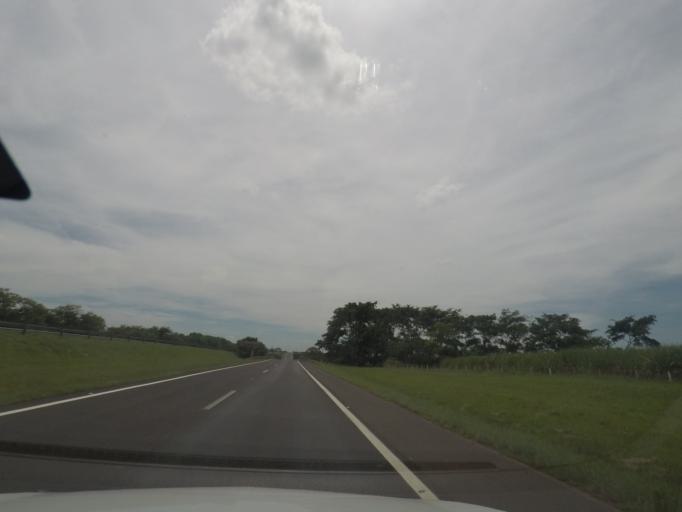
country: BR
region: Sao Paulo
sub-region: Bebedouro
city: Bebedouro
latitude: -20.9822
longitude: -48.4363
